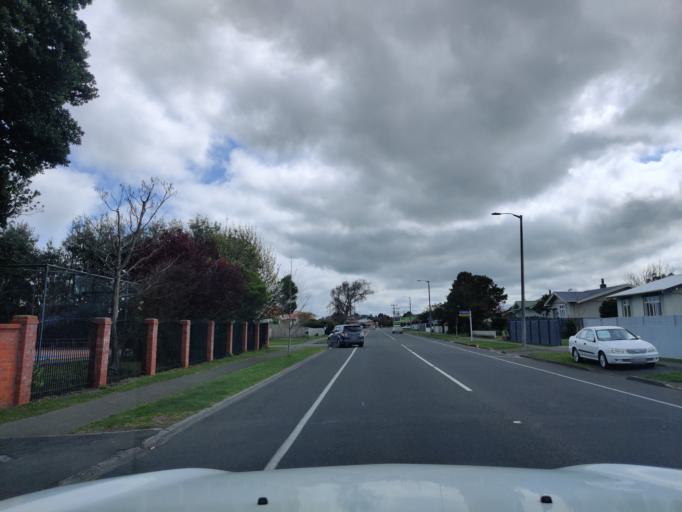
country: NZ
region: Manawatu-Wanganui
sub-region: Wanganui District
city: Wanganui
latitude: -39.9280
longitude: 175.0320
